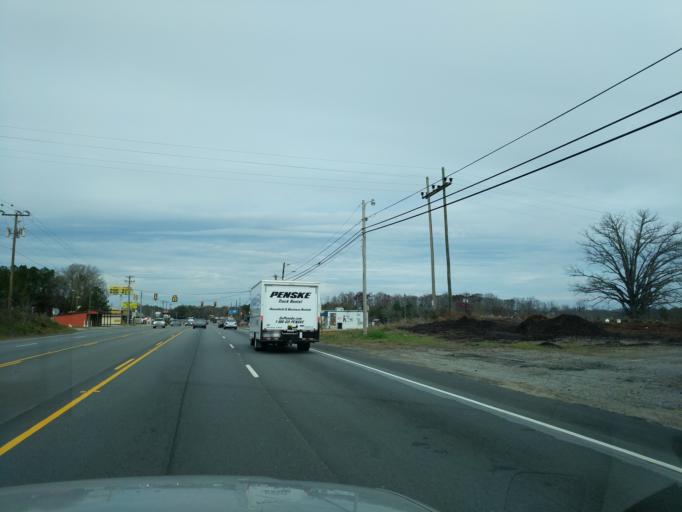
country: US
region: South Carolina
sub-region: Anderson County
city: Pendleton
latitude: 34.6280
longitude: -82.7806
